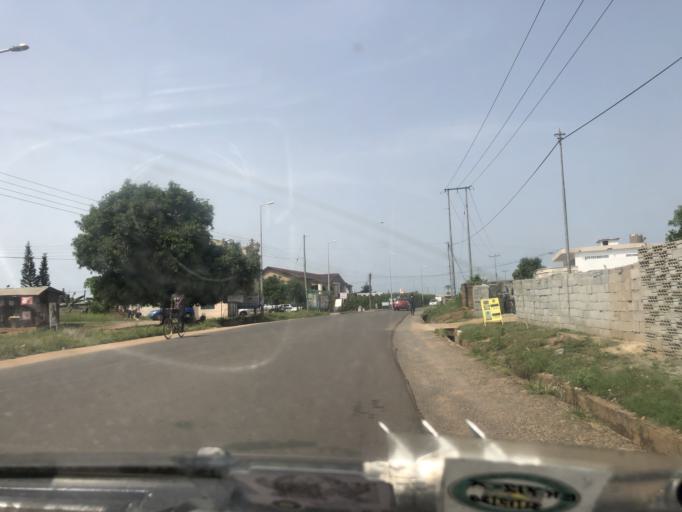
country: GH
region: Eastern
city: Koforidua
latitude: 6.0926
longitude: -0.2701
